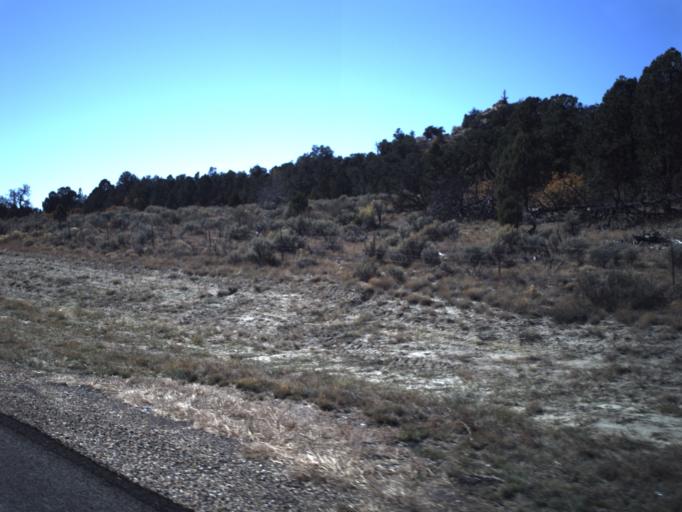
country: US
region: Utah
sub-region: Garfield County
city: Panguitch
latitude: 37.6531
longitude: -111.8403
